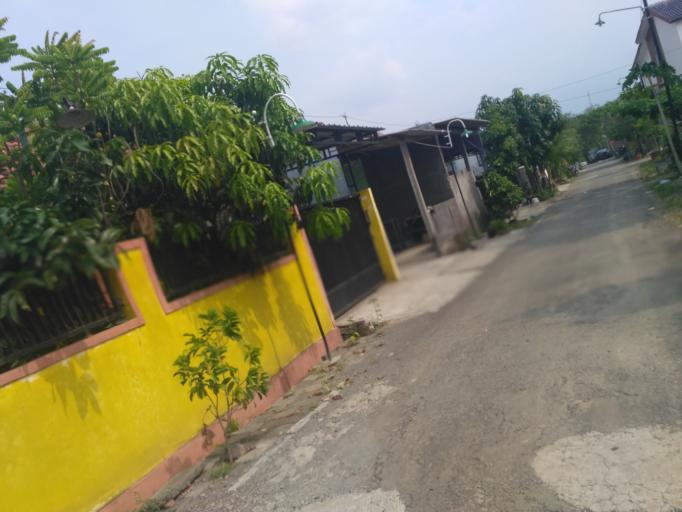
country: ID
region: Central Java
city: Mranggen
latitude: -7.0640
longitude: 110.4679
